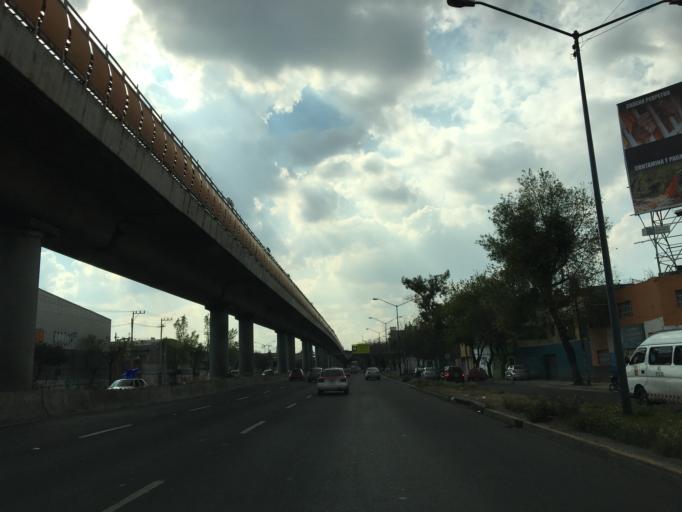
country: MX
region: Mexico City
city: Venustiano Carranza
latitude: 19.4386
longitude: -99.0994
